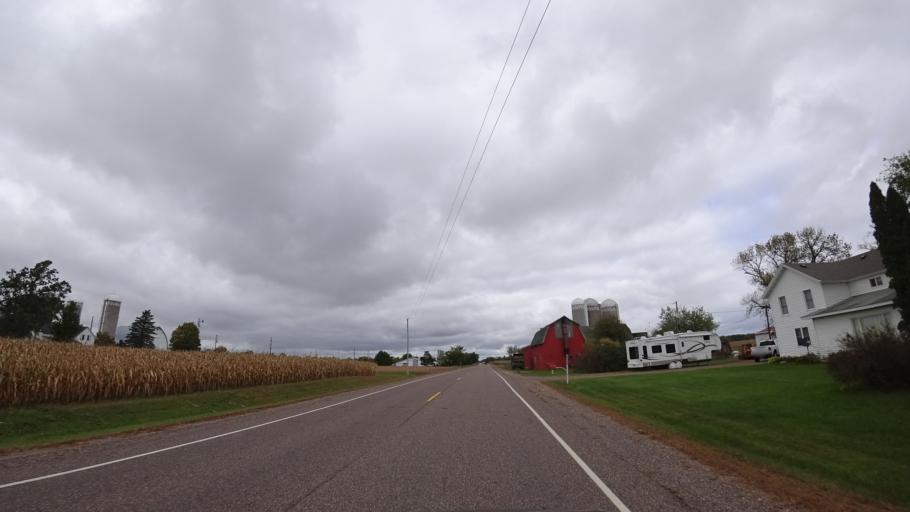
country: US
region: Wisconsin
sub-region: Chippewa County
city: Lake Wissota
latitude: 45.0075
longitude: -91.2867
